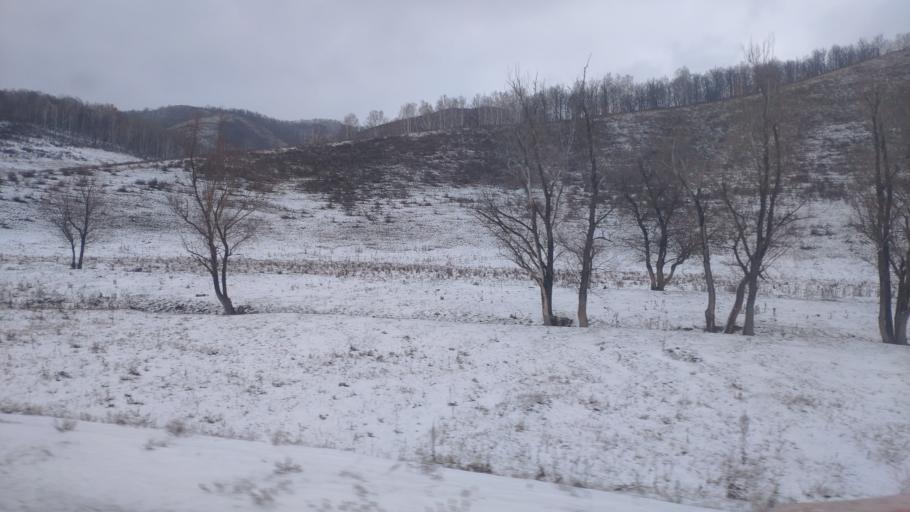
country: RU
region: Bashkortostan
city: Isyangulovo
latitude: 52.1618
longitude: 56.9088
